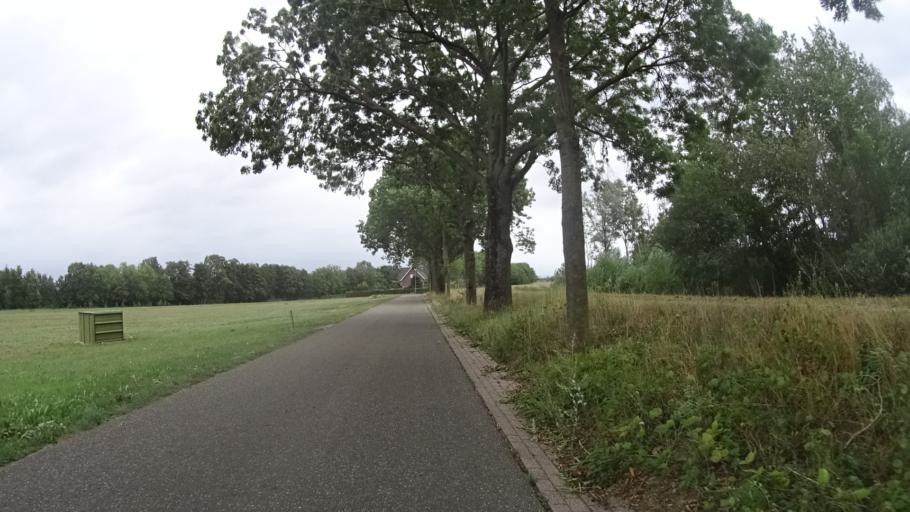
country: NL
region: Limburg
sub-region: Gemeente Venlo
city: Tegelen
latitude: 51.3497
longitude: 6.1298
